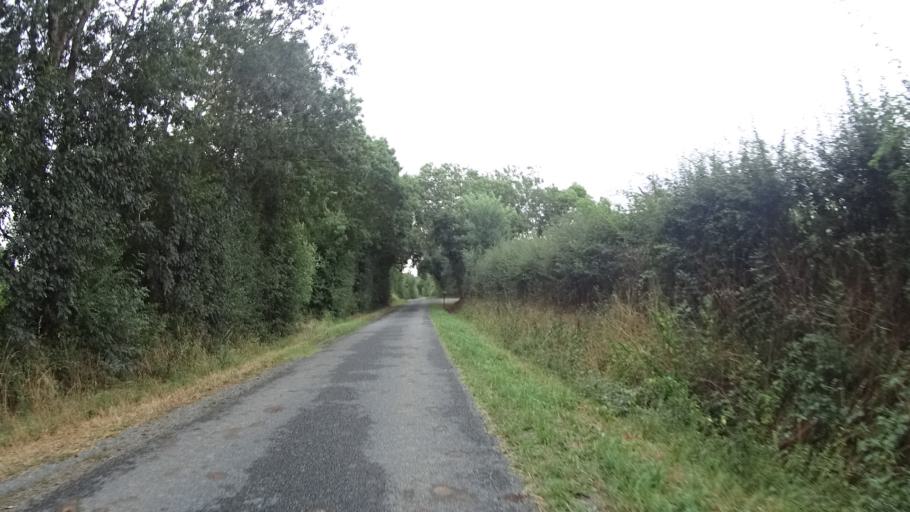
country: FR
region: Pays de la Loire
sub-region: Departement de Maine-et-Loire
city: La Chapelle-Saint-Florent
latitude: 47.3610
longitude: -1.0605
